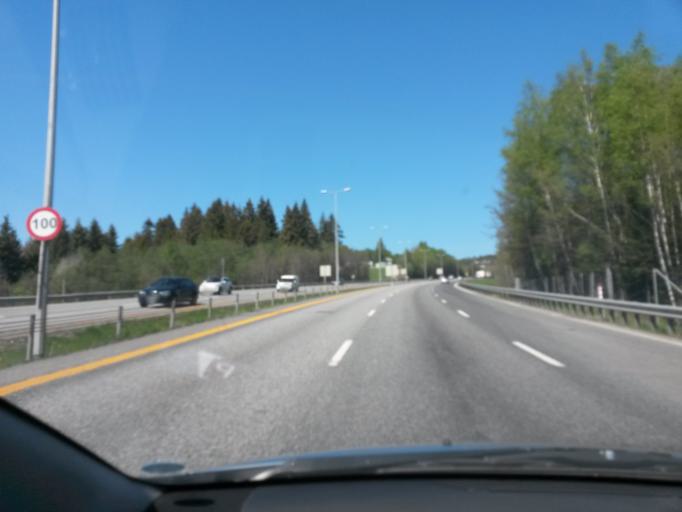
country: NO
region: Buskerud
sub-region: Lier
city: Tranby
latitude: 59.7985
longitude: 10.2679
